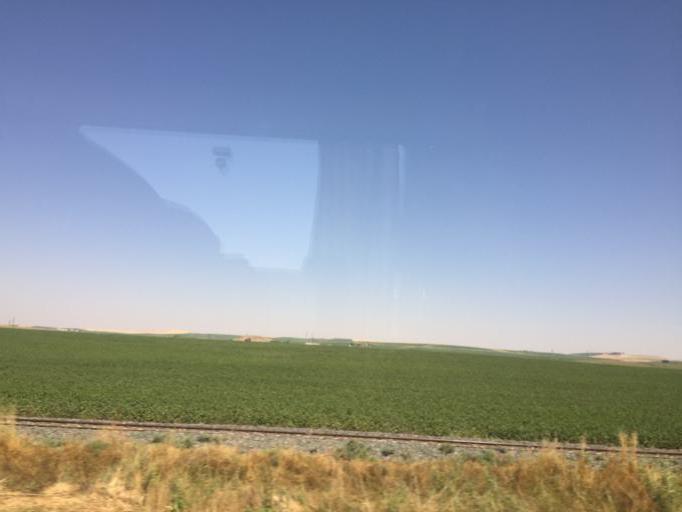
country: TR
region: Diyarbakir
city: Tepe
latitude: 37.8510
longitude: 40.7589
